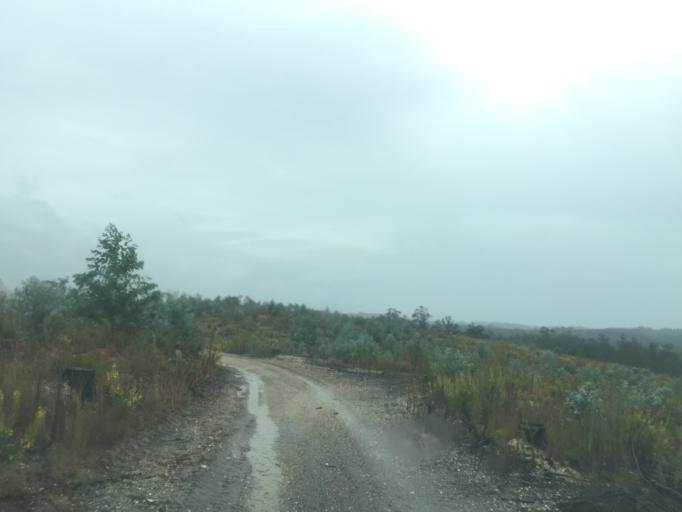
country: PT
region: Coimbra
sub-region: Figueira da Foz
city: Lavos
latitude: 40.0727
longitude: -8.7868
